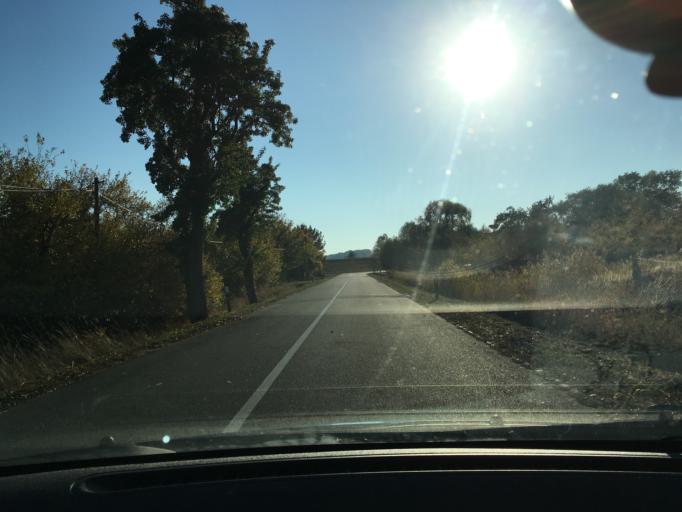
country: DE
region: Lower Saxony
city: Hitzacker
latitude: 53.1629
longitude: 11.0552
